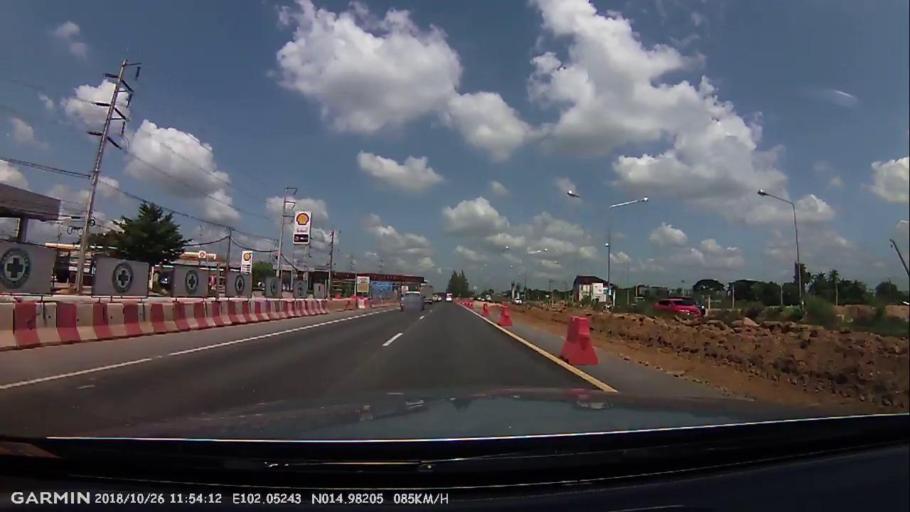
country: TH
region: Nakhon Ratchasima
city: Nakhon Ratchasima
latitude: 14.9822
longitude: 102.0525
